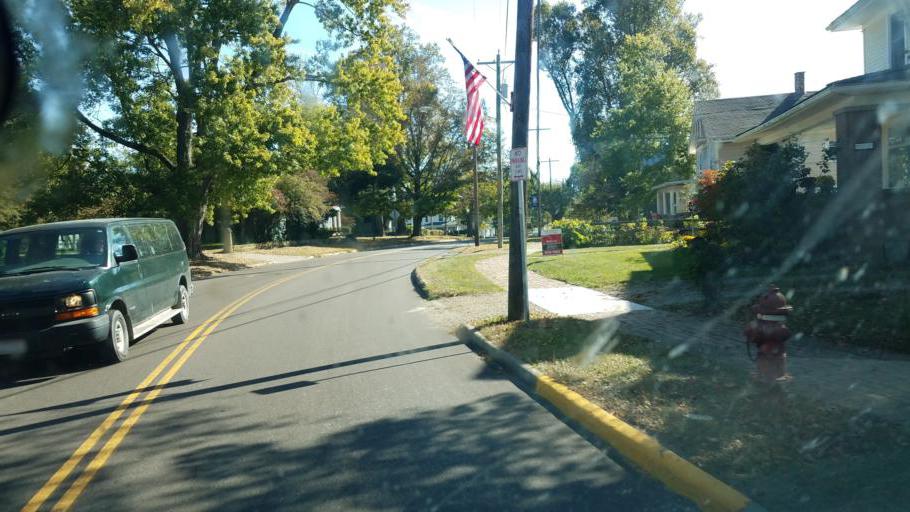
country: US
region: Ohio
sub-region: Knox County
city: Fredericktown
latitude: 40.4811
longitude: -82.5491
